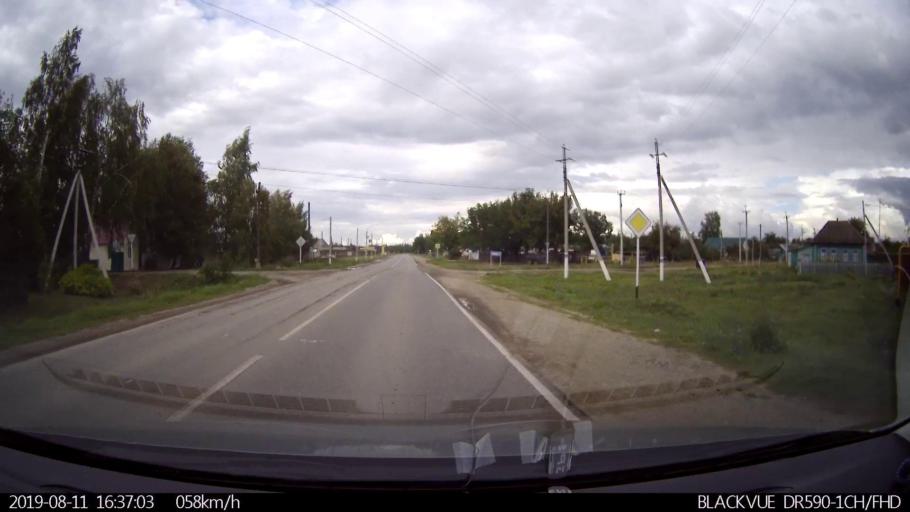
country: RU
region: Ulyanovsk
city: Mayna
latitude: 54.1241
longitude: 47.6119
